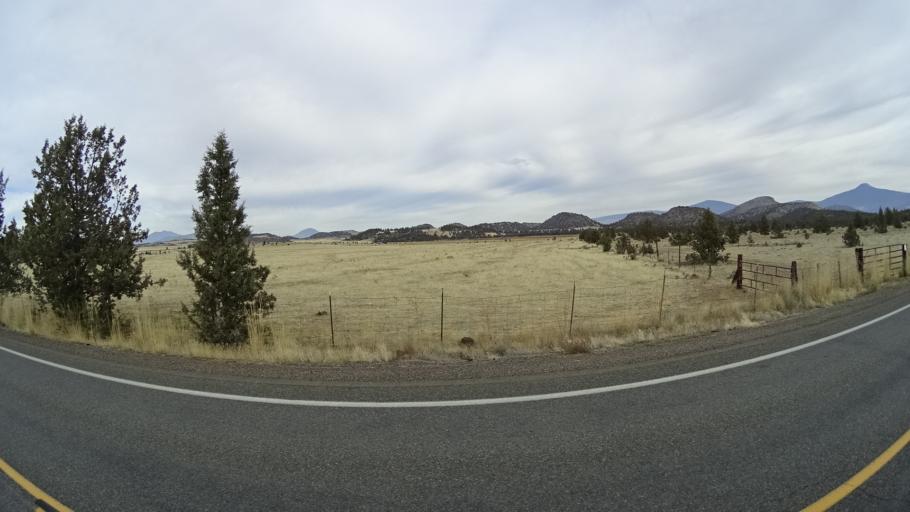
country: US
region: California
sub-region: Siskiyou County
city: Montague
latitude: 41.6399
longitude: -122.4663
